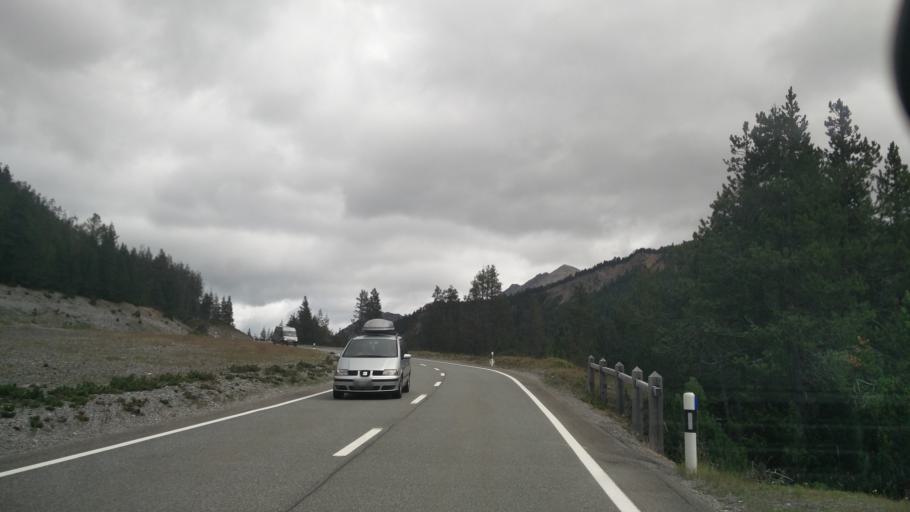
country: CH
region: Grisons
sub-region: Inn District
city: Scuol
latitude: 46.6577
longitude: 10.2433
